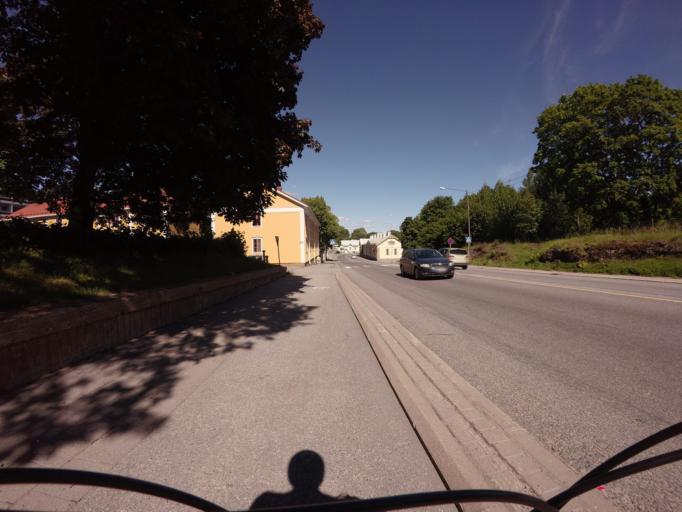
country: FI
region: Varsinais-Suomi
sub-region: Turku
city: Turku
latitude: 60.4592
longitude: 22.2595
